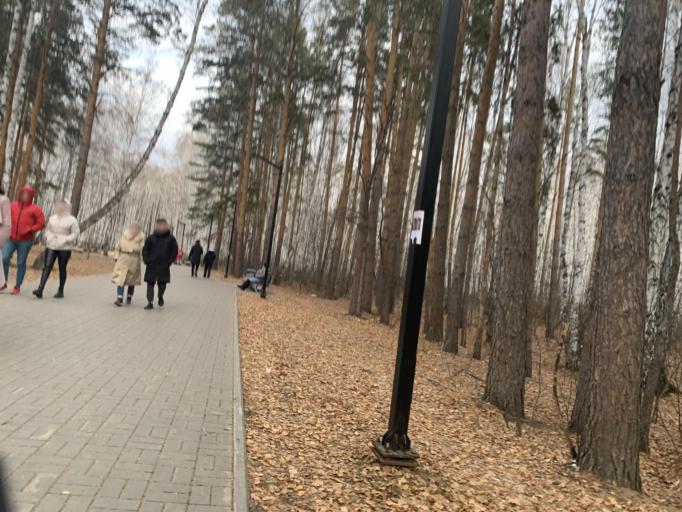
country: RU
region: Chelyabinsk
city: Roshchino
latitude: 55.1953
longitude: 61.2902
